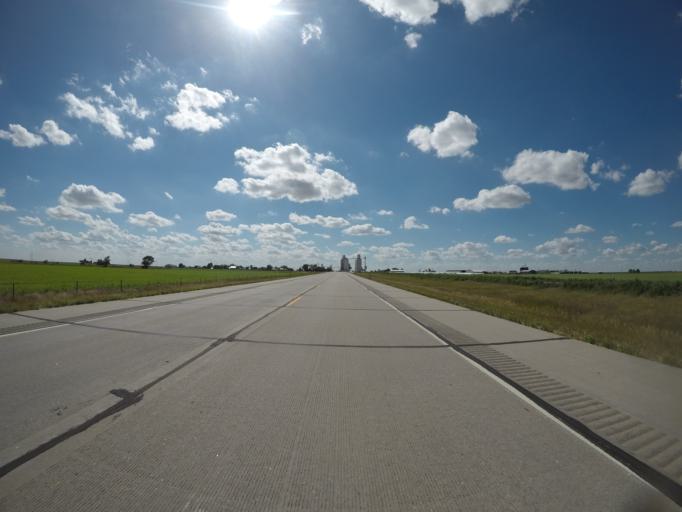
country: US
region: Colorado
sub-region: Phillips County
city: Holyoke
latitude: 40.6112
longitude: -102.4633
